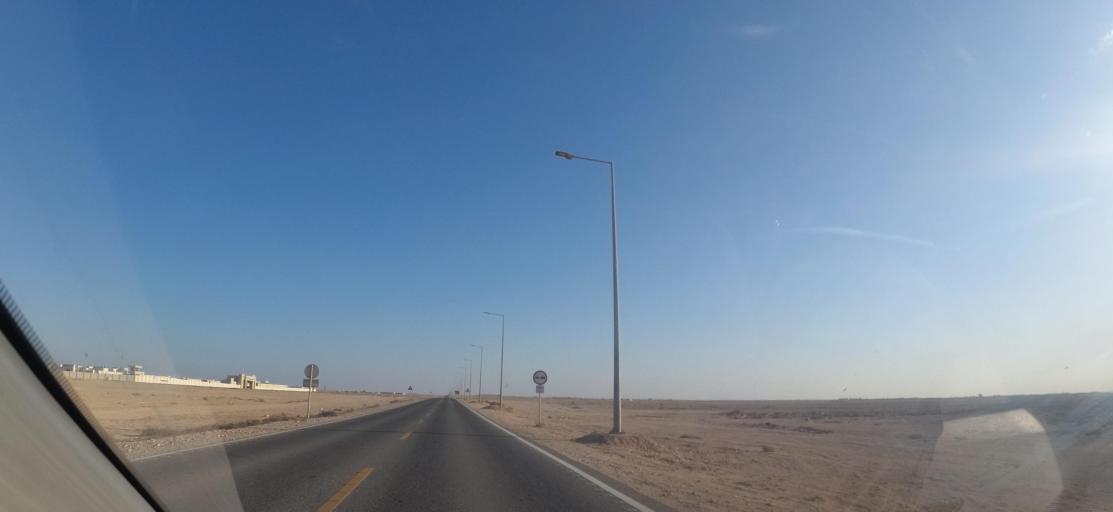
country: QA
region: Madinat ash Shamal
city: Ar Ru'ays
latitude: 26.1312
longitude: 51.2321
